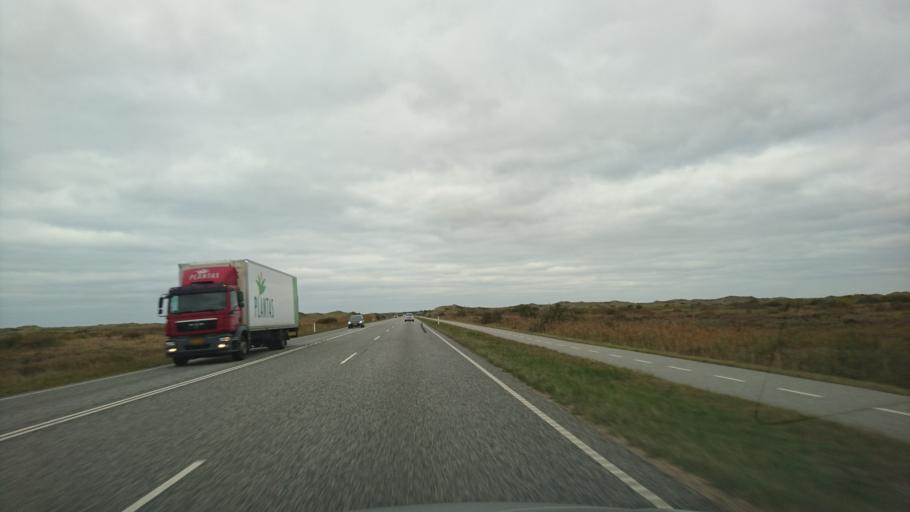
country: DK
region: North Denmark
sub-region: Frederikshavn Kommune
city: Skagen
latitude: 57.6797
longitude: 10.4618
